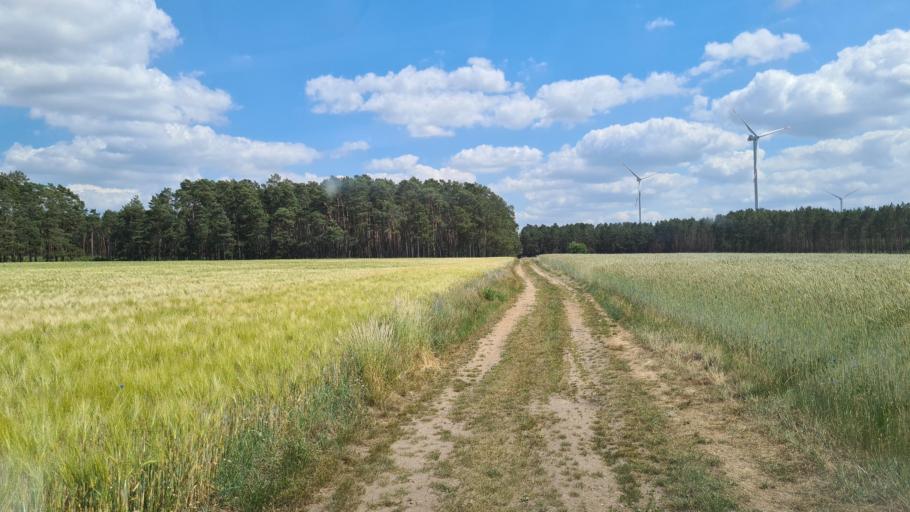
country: DE
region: Brandenburg
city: Sallgast
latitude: 51.6537
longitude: 13.8148
